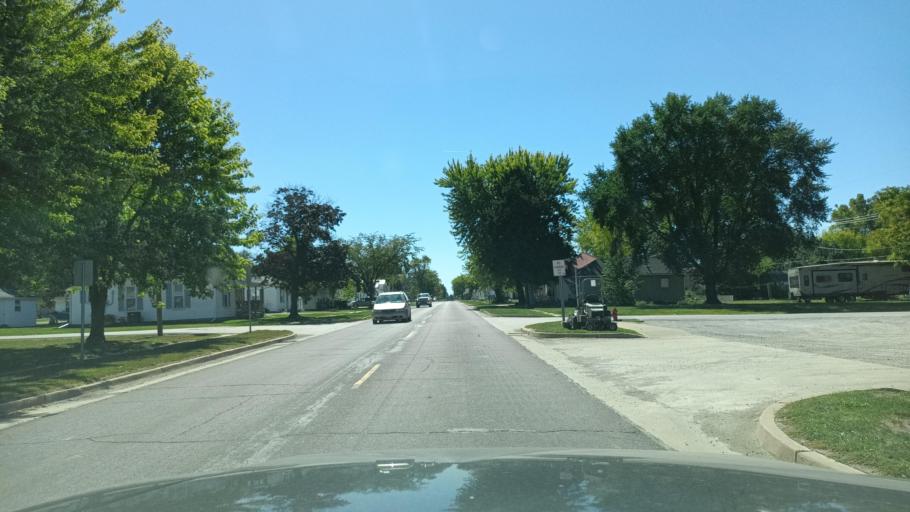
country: US
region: Missouri
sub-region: Macon County
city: La Plata
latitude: 40.0278
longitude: -92.4885
